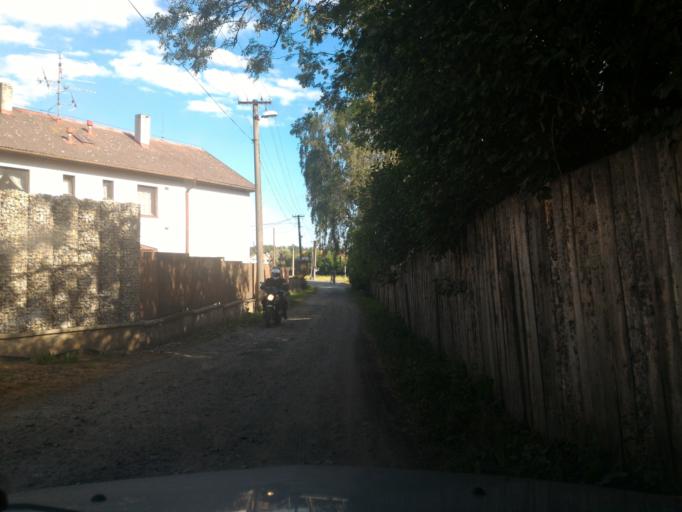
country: CZ
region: Vysocina
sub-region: Okres Jihlava
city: Telc
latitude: 49.1932
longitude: 15.4501
